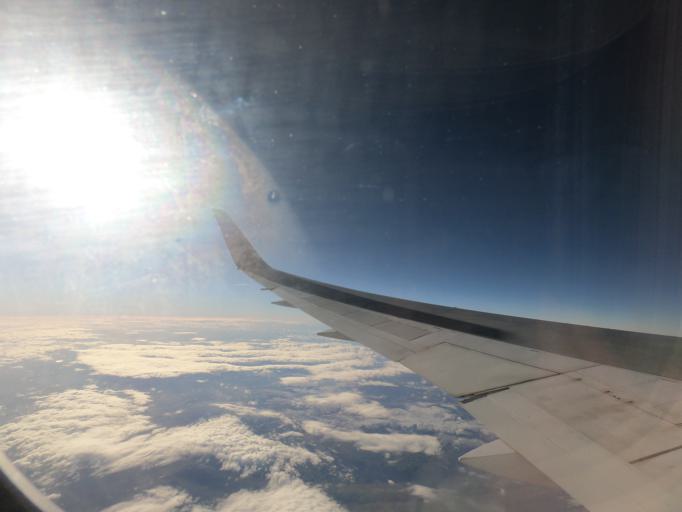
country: GB
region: England
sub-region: City and Borough of Leeds
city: Morley
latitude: 53.7339
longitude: -1.5883
